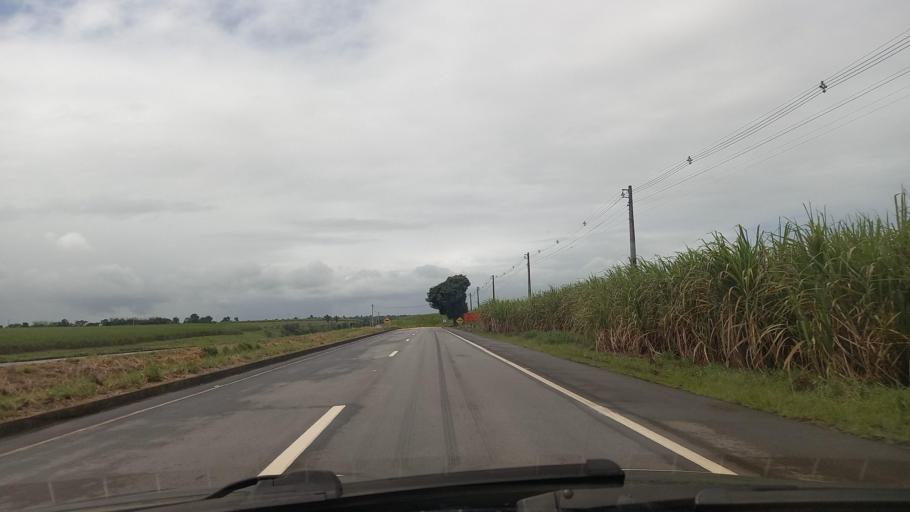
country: BR
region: Alagoas
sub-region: Campo Alegre
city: Campo Alegre
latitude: -9.8230
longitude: -36.2346
